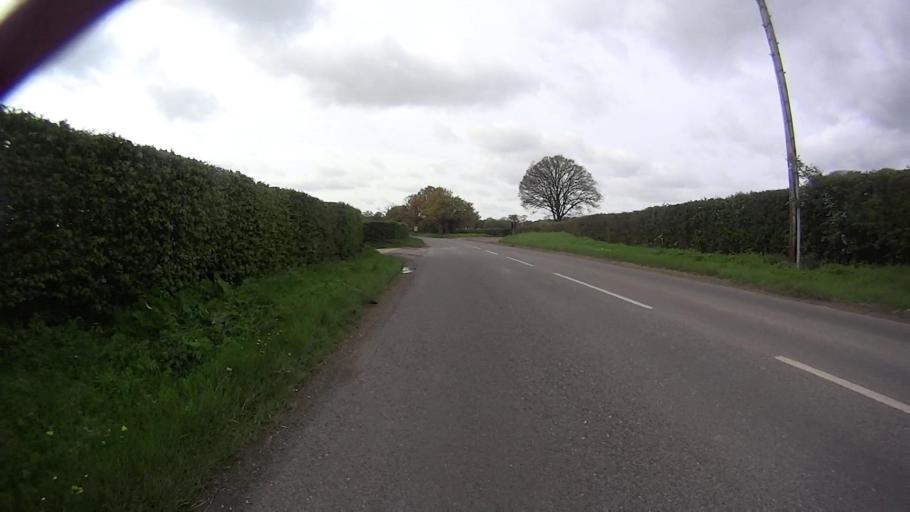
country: GB
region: England
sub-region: West Sussex
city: Horsham
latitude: 51.1095
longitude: -0.2960
